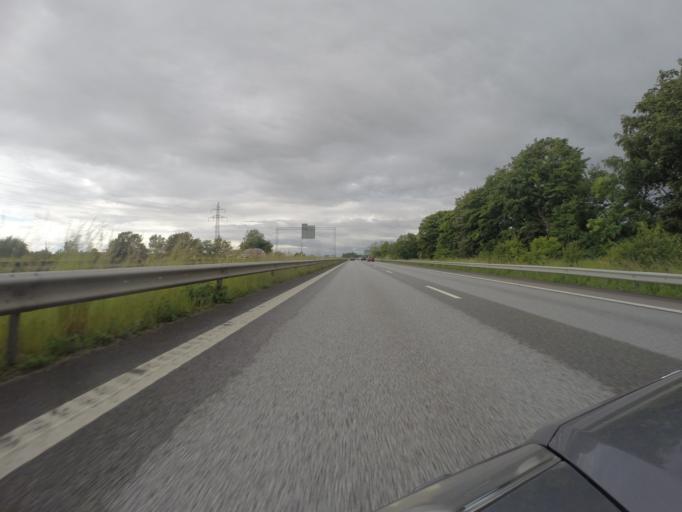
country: SE
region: Skane
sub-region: Lomma Kommun
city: Lomma
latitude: 55.6634
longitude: 13.0994
